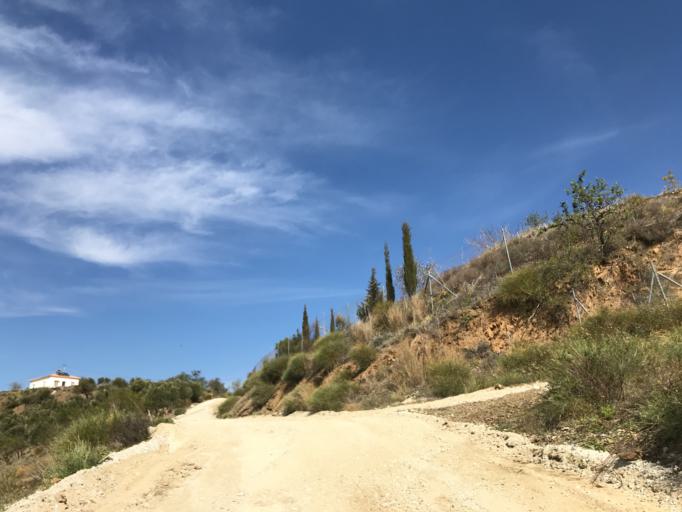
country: ES
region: Andalusia
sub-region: Provincia de Malaga
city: Valdes
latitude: 36.7747
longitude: -4.2176
